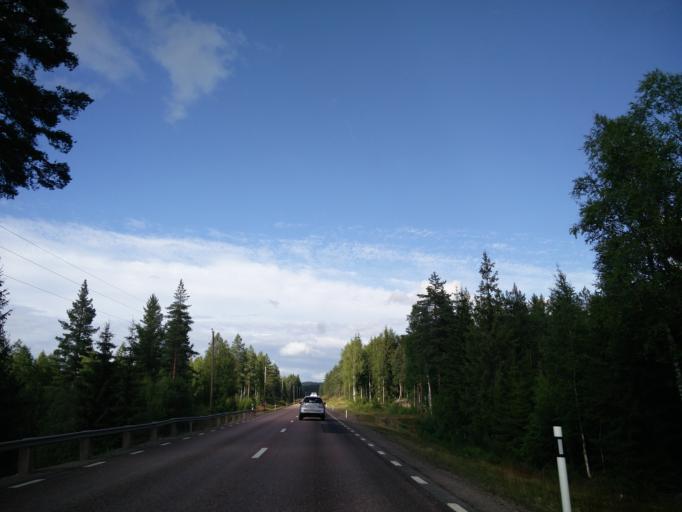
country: SE
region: Vaermland
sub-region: Hagfors Kommun
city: Ekshaerad
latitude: 60.4410
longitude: 13.2687
